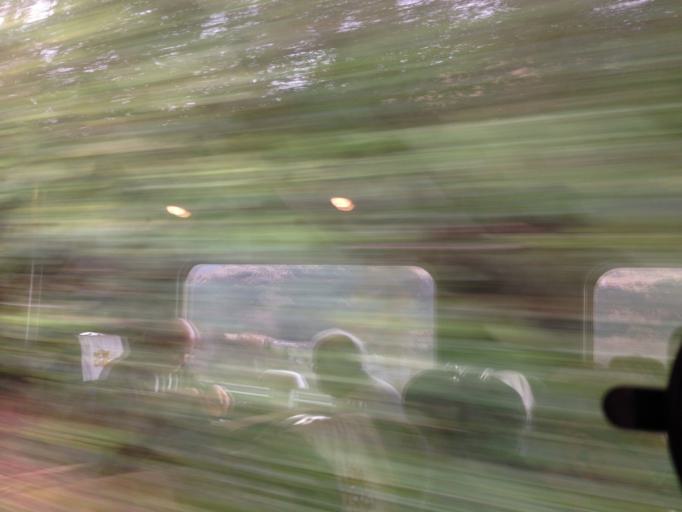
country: GB
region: Scotland
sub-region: Argyll and Bute
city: Garelochhead
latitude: 56.1937
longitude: -4.7435
